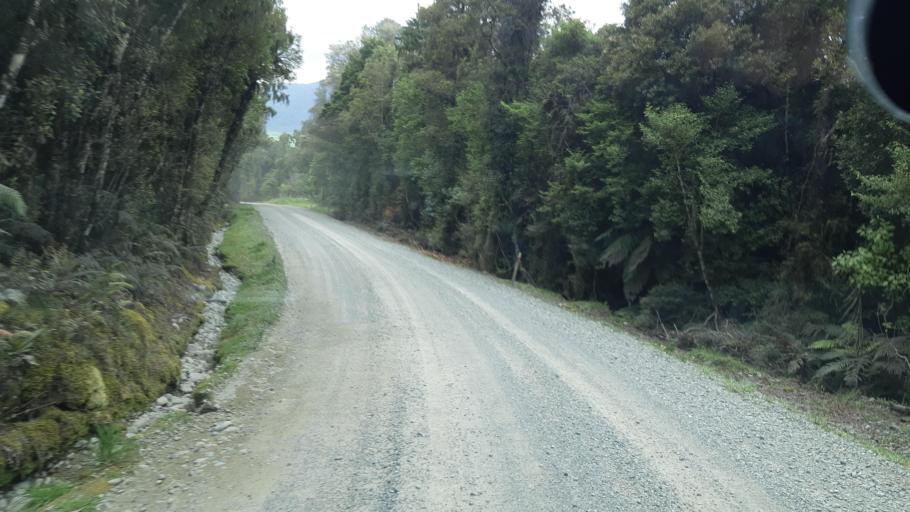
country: NZ
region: West Coast
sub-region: Grey District
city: Greymouth
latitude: -42.7243
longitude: 171.2418
